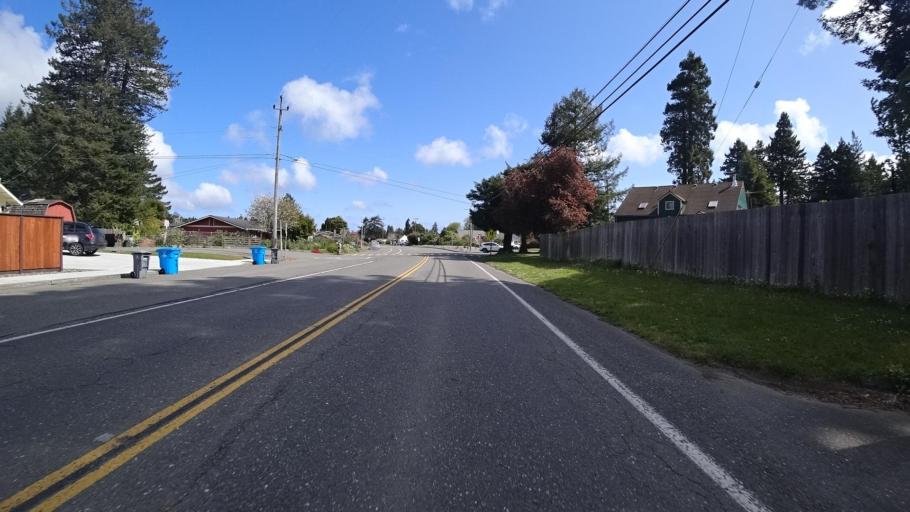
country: US
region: California
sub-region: Humboldt County
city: Pine Hills
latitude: 40.7366
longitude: -124.1480
